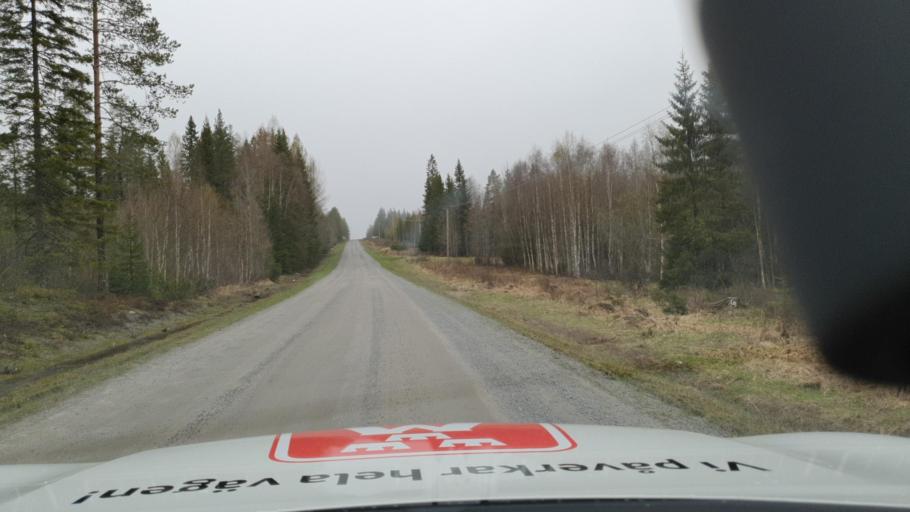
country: SE
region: Vaesterbotten
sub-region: Nordmalings Kommun
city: Nordmaling
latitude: 63.7381
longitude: 19.5038
